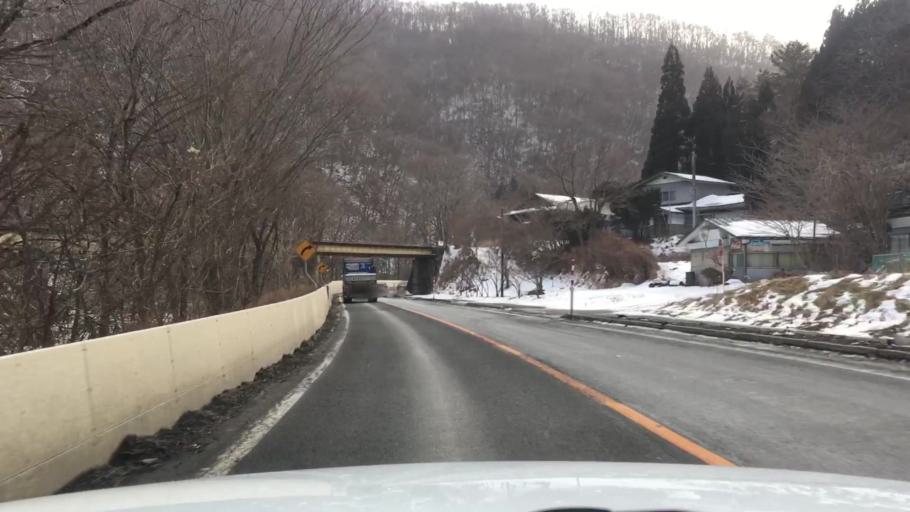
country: JP
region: Iwate
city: Tono
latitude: 39.6257
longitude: 141.5138
